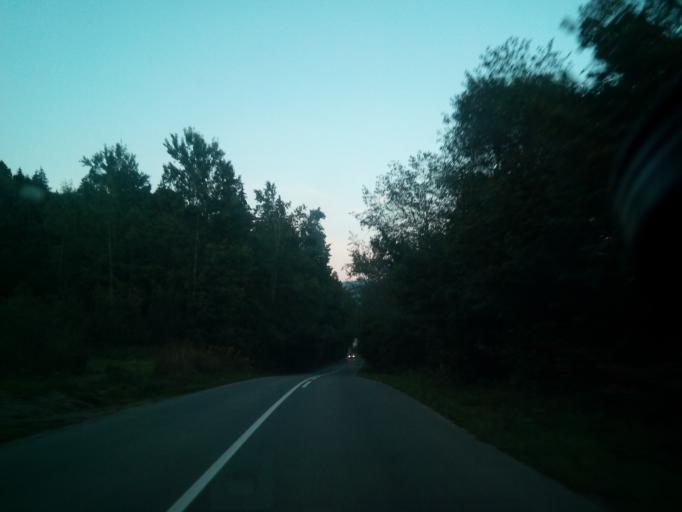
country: SK
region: Kosicky
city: Dobsina
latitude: 48.7914
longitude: 20.3518
